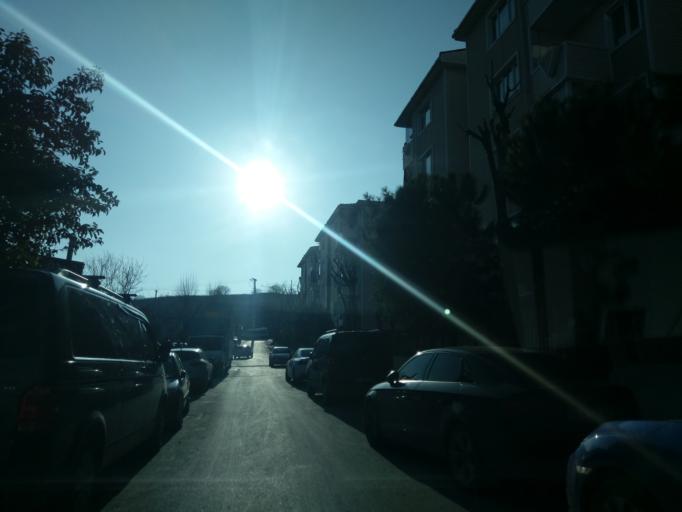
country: TR
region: Istanbul
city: Mahmutbey
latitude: 41.0353
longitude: 28.7647
